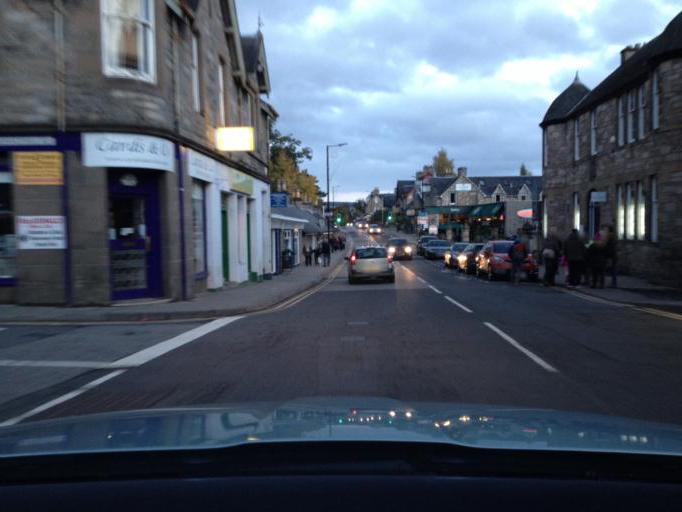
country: GB
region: Scotland
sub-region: Perth and Kinross
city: Pitlochry
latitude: 56.7027
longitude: -3.7330
